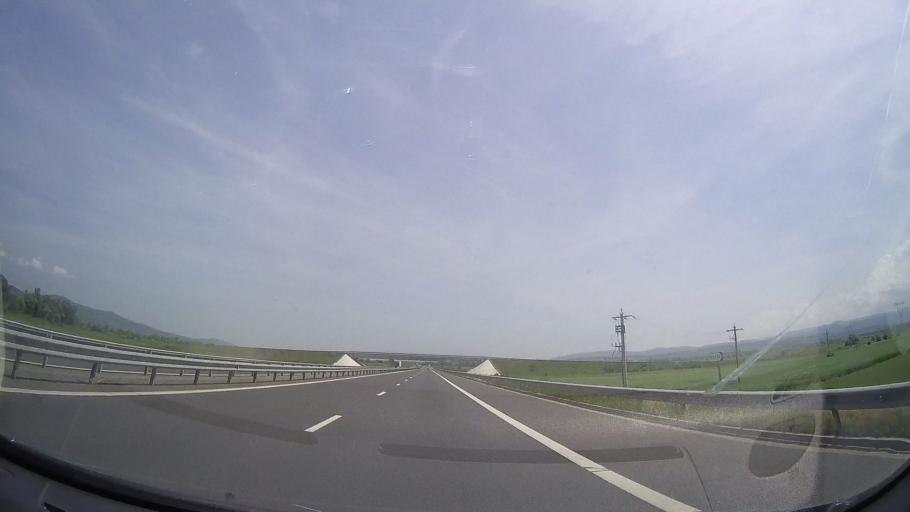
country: RO
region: Hunedoara
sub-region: Comuna Geoagiu
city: Geoagiu
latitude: 45.8818
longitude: 23.2180
